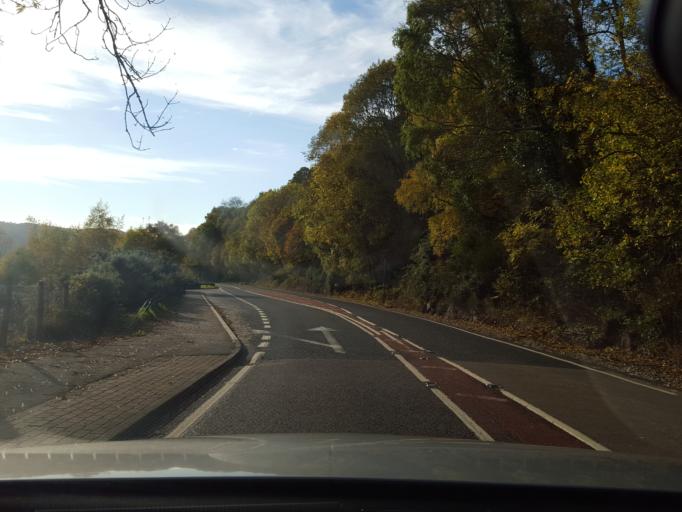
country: GB
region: Scotland
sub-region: Highland
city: Beauly
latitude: 57.3259
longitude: -4.4452
